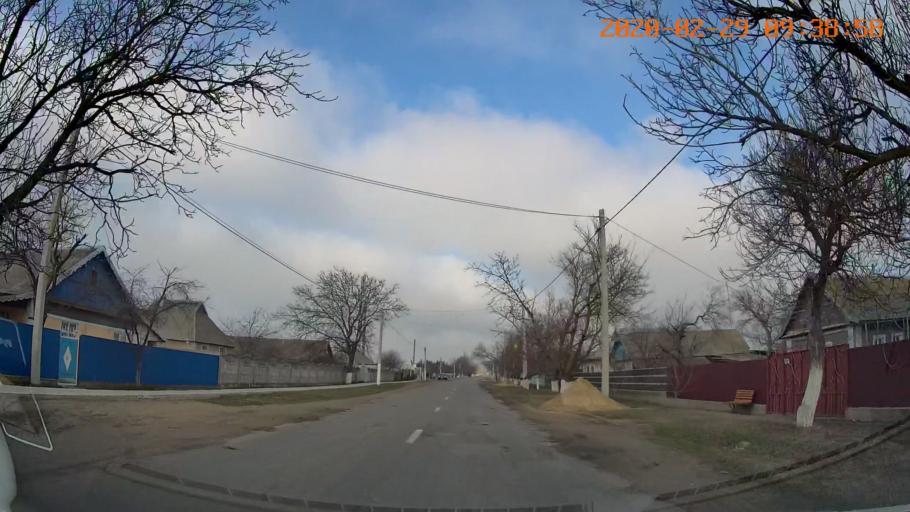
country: MD
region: Telenesti
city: Crasnoe
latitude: 46.6333
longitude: 29.8602
